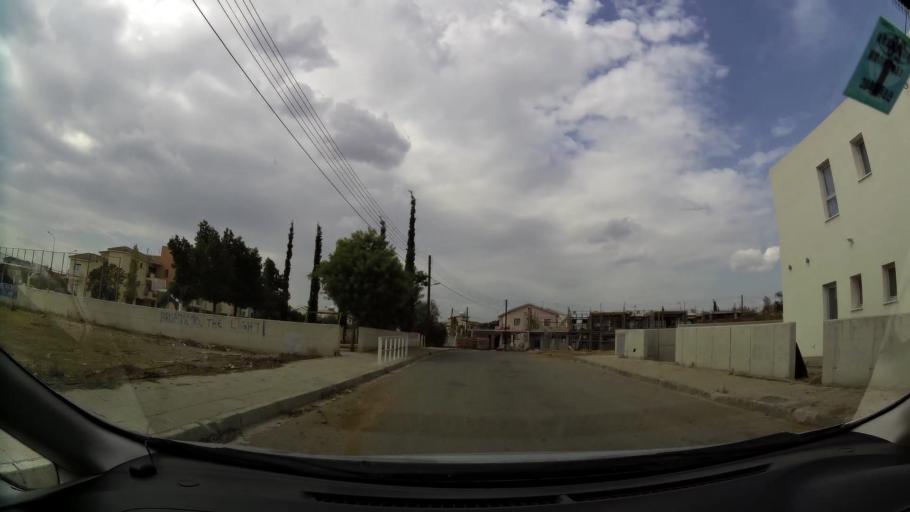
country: CY
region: Lefkosia
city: Geri
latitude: 35.1129
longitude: 33.3703
